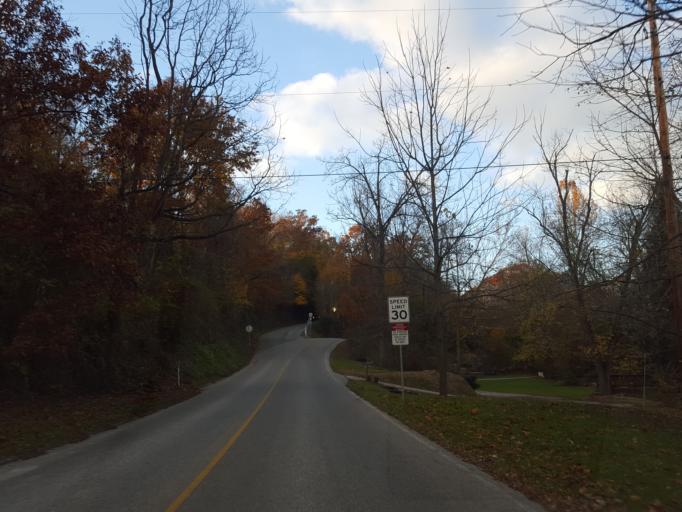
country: US
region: Pennsylvania
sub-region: York County
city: Dallastown
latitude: 39.8825
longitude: -76.6714
